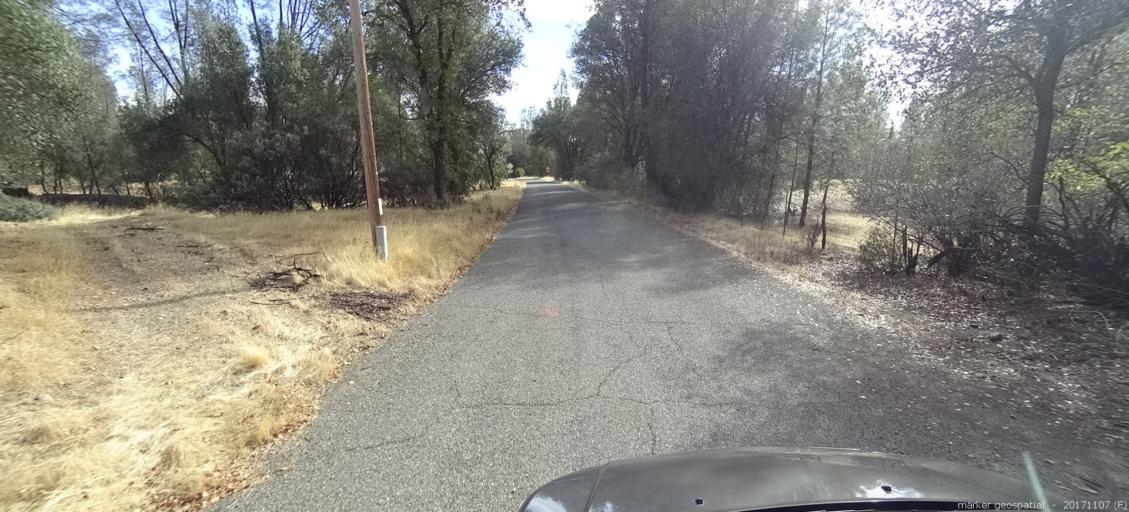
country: US
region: California
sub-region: Shasta County
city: Shasta
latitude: 40.4098
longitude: -122.5227
